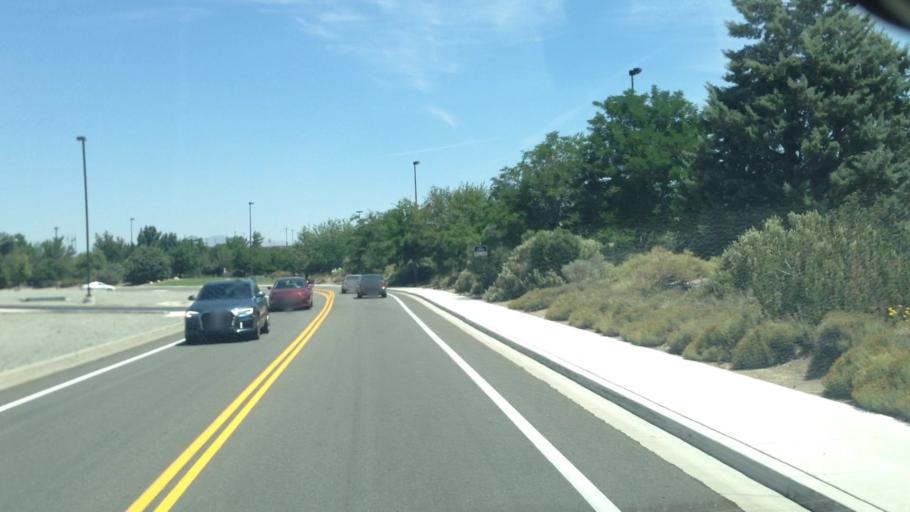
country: US
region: Nevada
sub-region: Washoe County
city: Sparks
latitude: 39.5031
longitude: -119.7798
